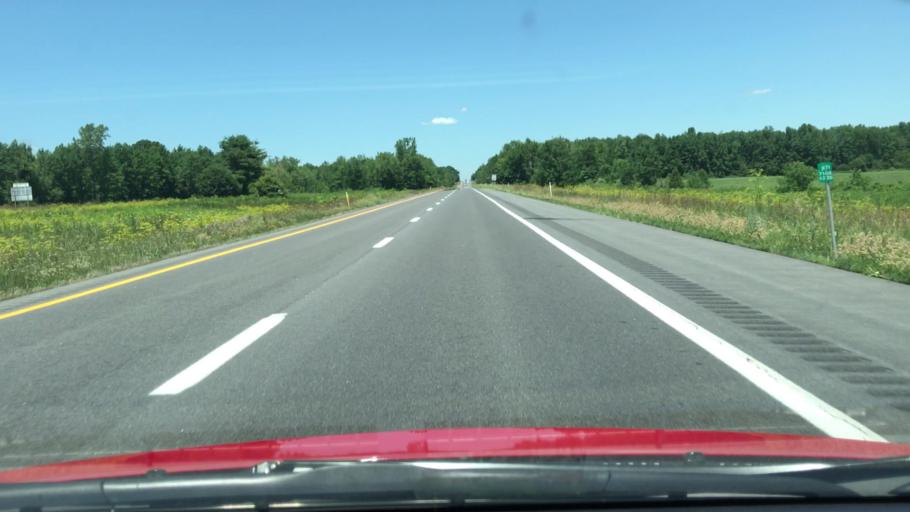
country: US
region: New York
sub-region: Clinton County
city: Cumberland Head
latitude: 44.7904
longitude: -73.4399
